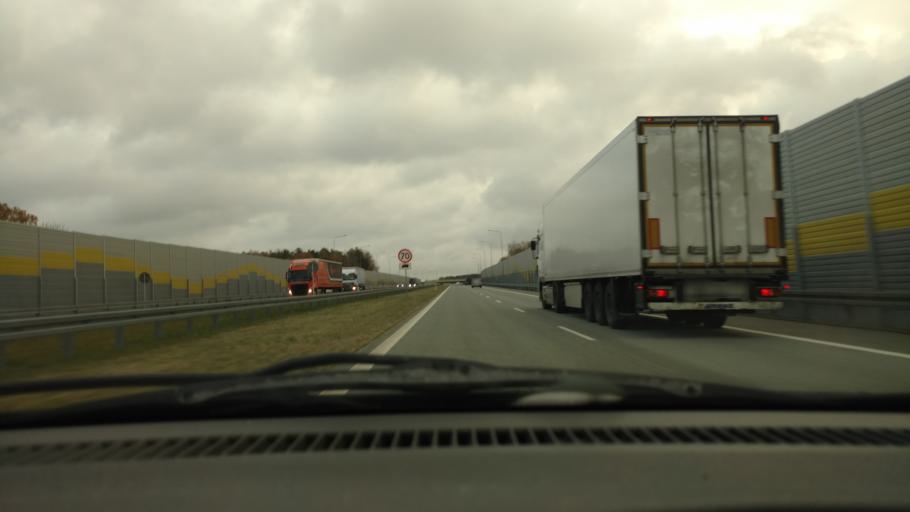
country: PL
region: Lodz Voivodeship
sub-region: Powiat pabianicki
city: Ksawerow
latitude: 51.6322
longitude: 19.4258
